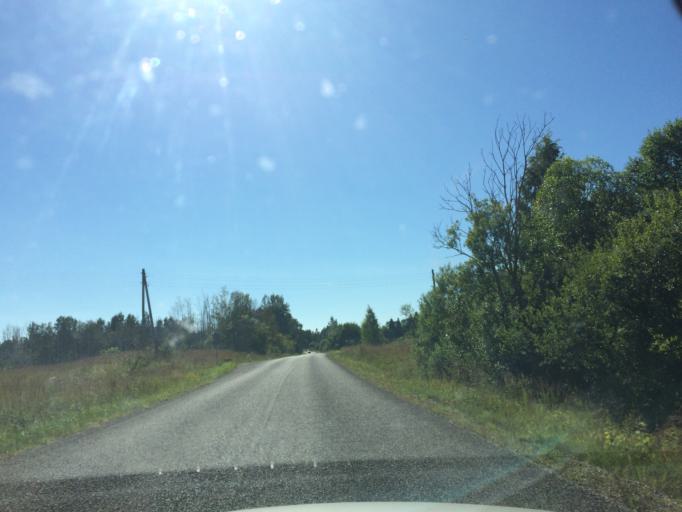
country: LV
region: Rezekne
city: Rezekne
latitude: 56.4950
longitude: 27.2812
